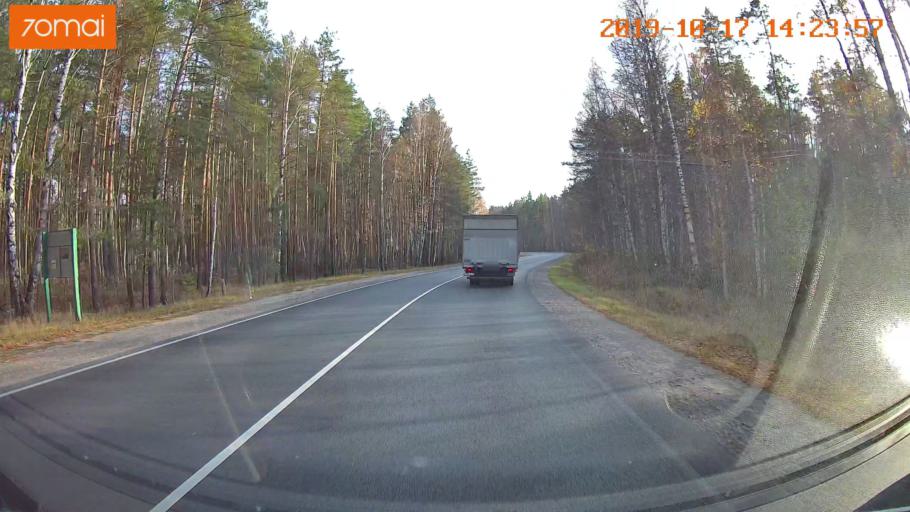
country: RU
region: Moskovskaya
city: Radovitskiy
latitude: 55.0135
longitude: 39.9637
